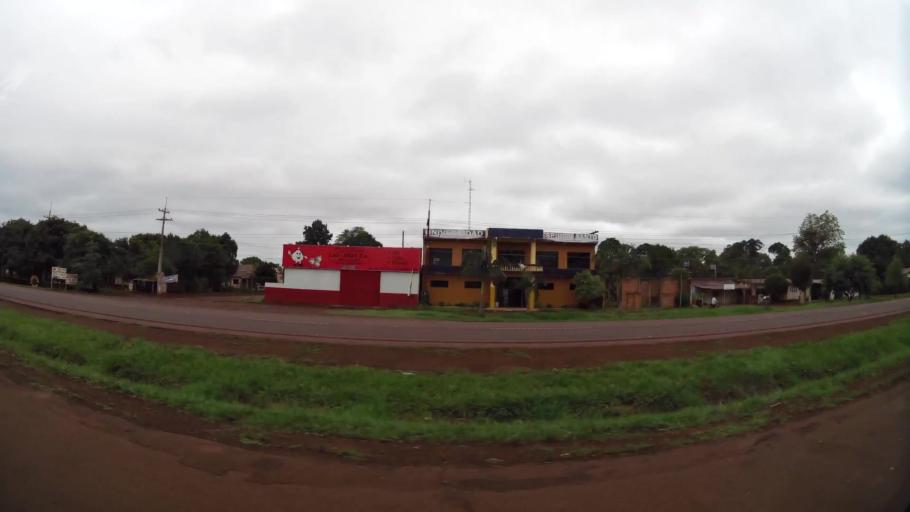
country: PY
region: Alto Parana
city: Los Cedrales
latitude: -25.4889
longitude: -54.8062
